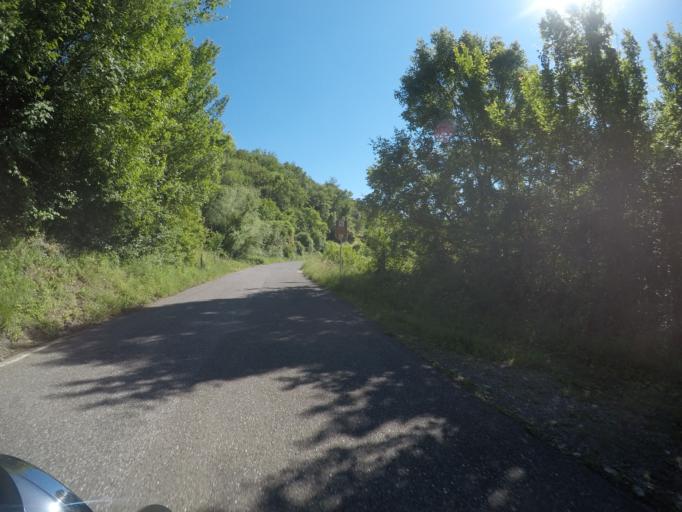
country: IT
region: Tuscany
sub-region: Provincia di Massa-Carrara
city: Fosdinovo
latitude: 44.1488
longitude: 10.1016
